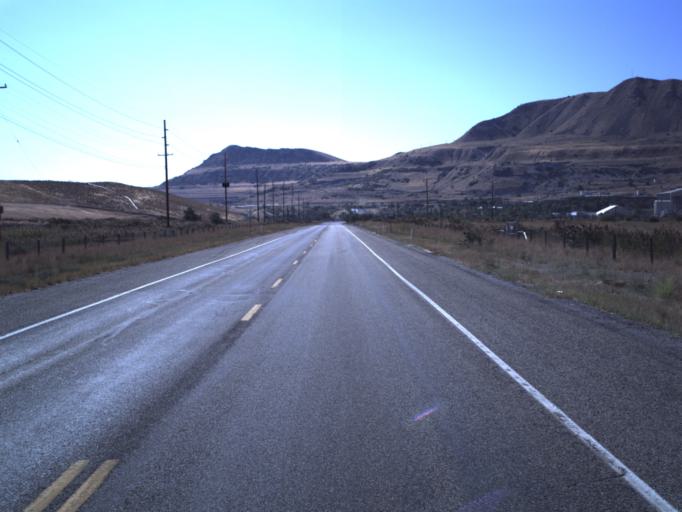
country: US
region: Utah
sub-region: Salt Lake County
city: Magna
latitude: 40.7375
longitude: -112.1740
